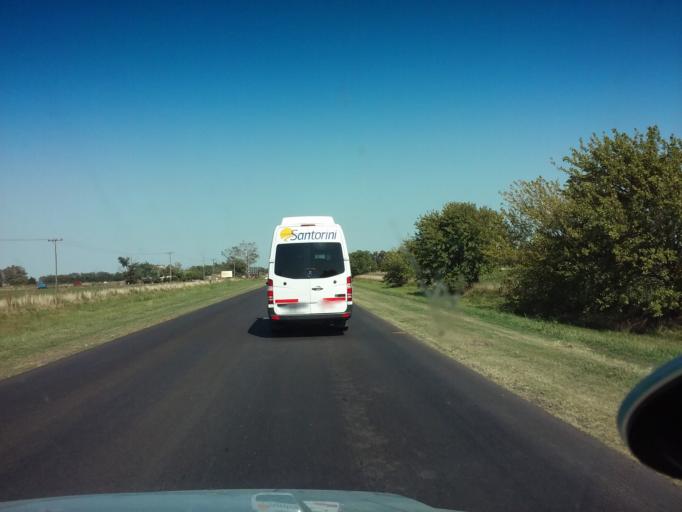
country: AR
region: Buenos Aires
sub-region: Partido de Chivilcoy
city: Chivilcoy
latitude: -34.9588
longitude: -60.0369
